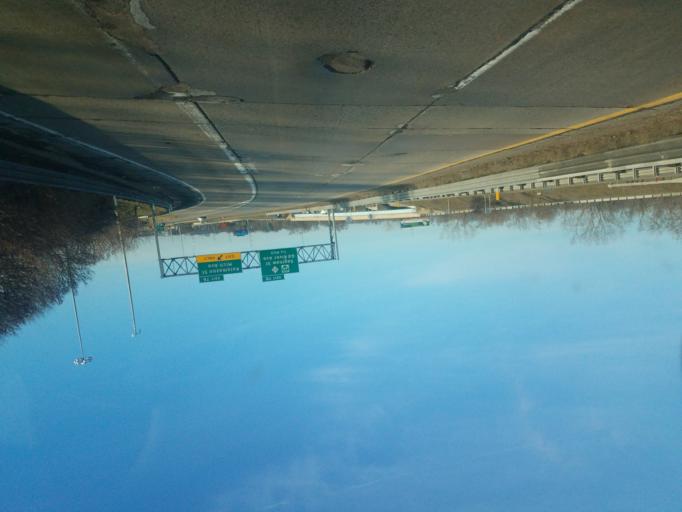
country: US
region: Michigan
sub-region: Ingham County
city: East Lansing
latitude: 42.7264
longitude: -84.5097
